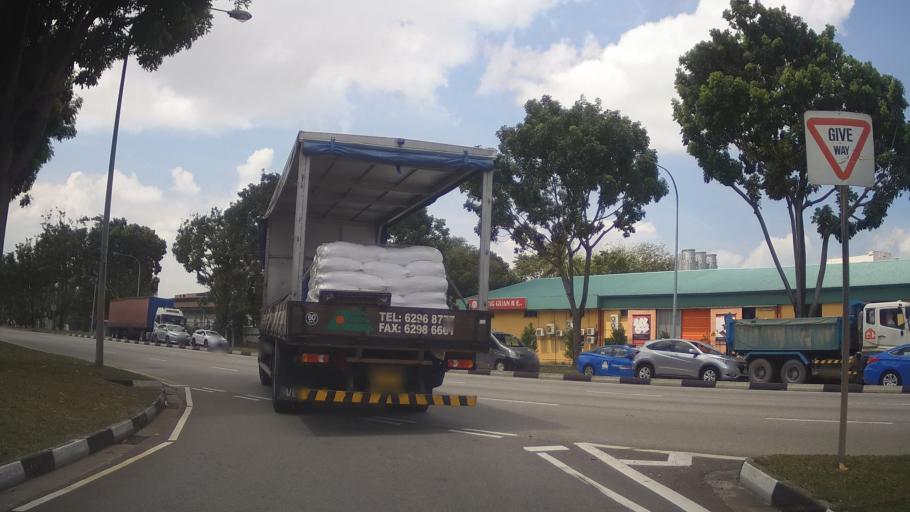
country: MY
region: Johor
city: Johor Bahru
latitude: 1.3363
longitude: 103.7096
